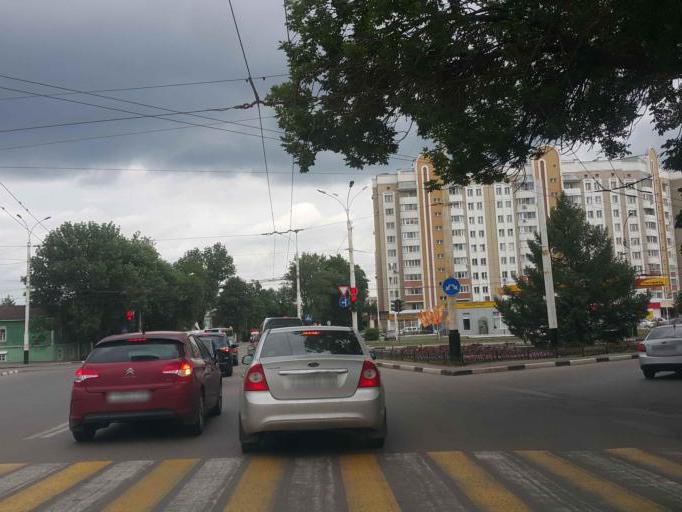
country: RU
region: Tambov
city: Tambov
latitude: 52.7364
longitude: 41.4407
